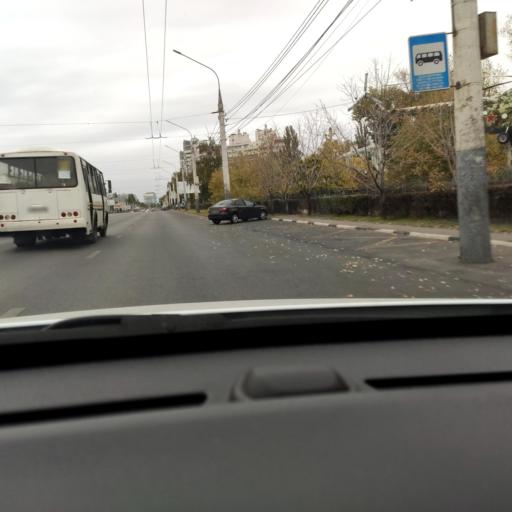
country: RU
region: Voronezj
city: Voronezh
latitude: 51.6596
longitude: 39.2461
